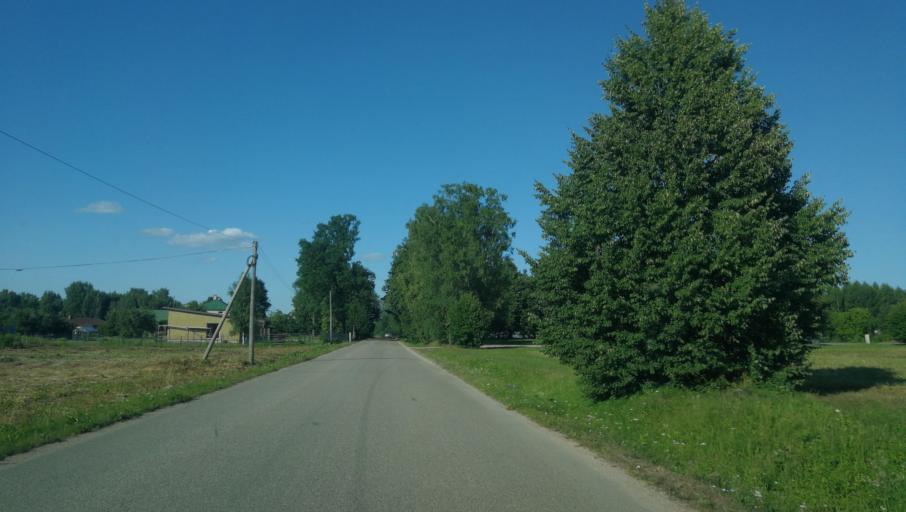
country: LV
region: Cesu Rajons
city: Cesis
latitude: 57.2969
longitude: 25.2368
